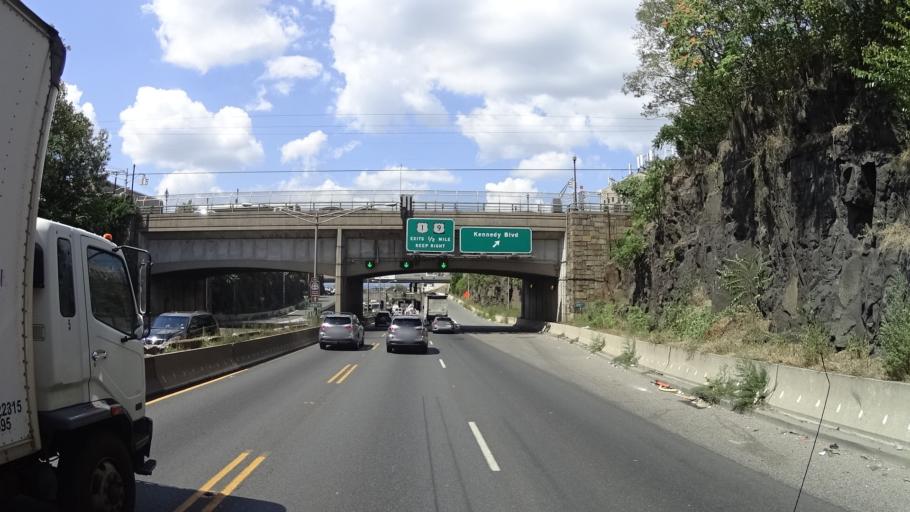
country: US
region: New Jersey
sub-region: Hudson County
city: Union City
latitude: 40.7727
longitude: -74.0324
